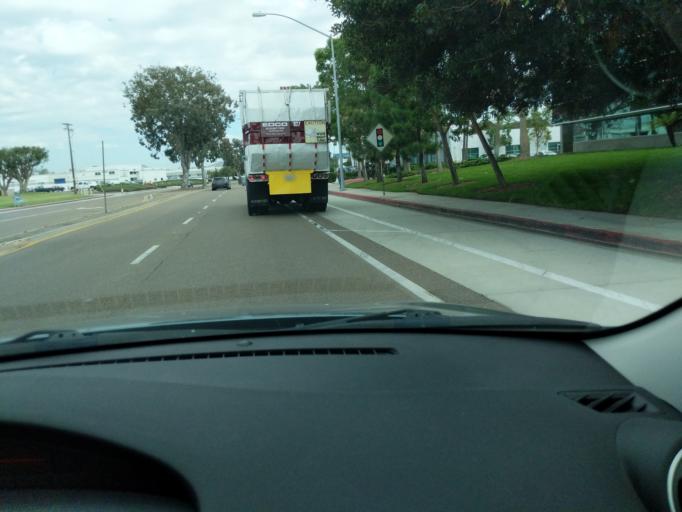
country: US
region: California
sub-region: San Diego County
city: San Diego
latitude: 32.8216
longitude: -117.1353
